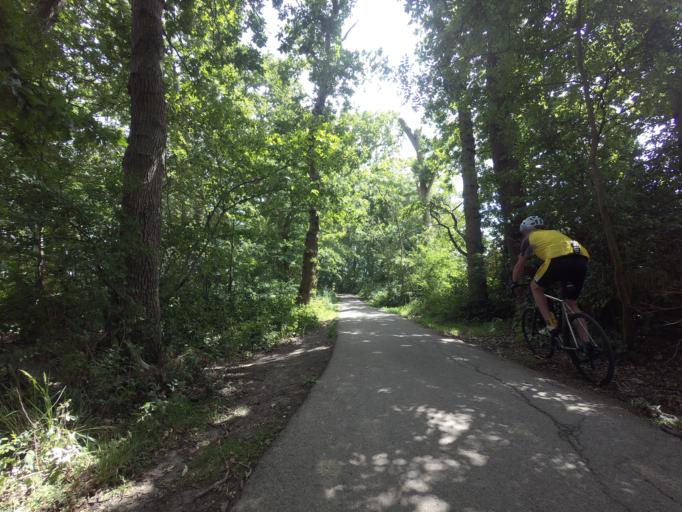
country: GB
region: England
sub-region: East Sussex
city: Hailsham
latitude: 50.8255
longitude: 0.2501
